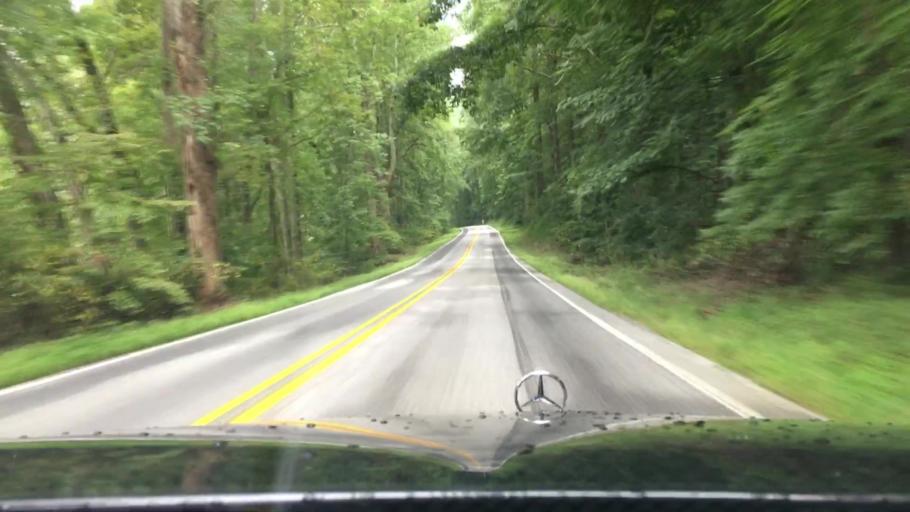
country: US
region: Virginia
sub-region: Nelson County
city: Nellysford
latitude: 37.8421
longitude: -78.9277
